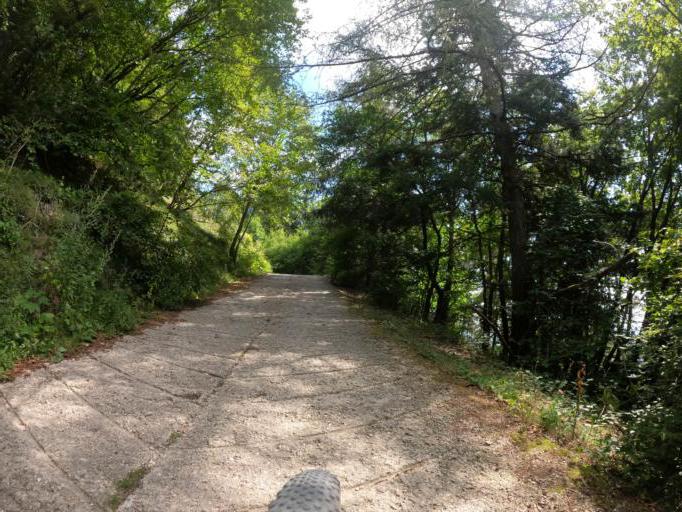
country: IT
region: Veneto
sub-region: Provincia di Verona
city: Ferrara di Monte Baldo
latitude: 45.6544
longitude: 10.8286
